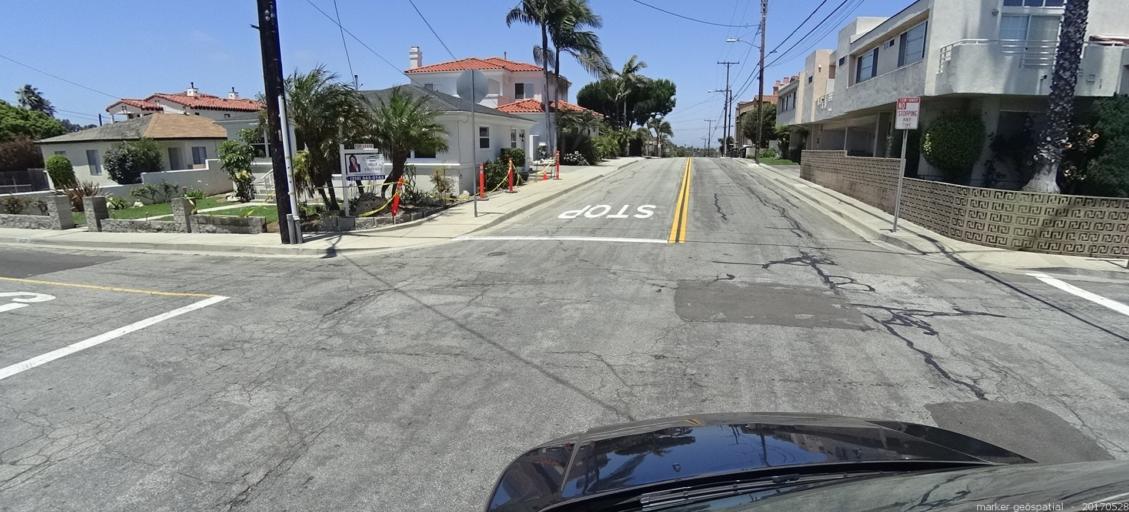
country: US
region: California
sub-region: Los Angeles County
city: Redondo Beach
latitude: 33.8633
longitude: -118.3812
